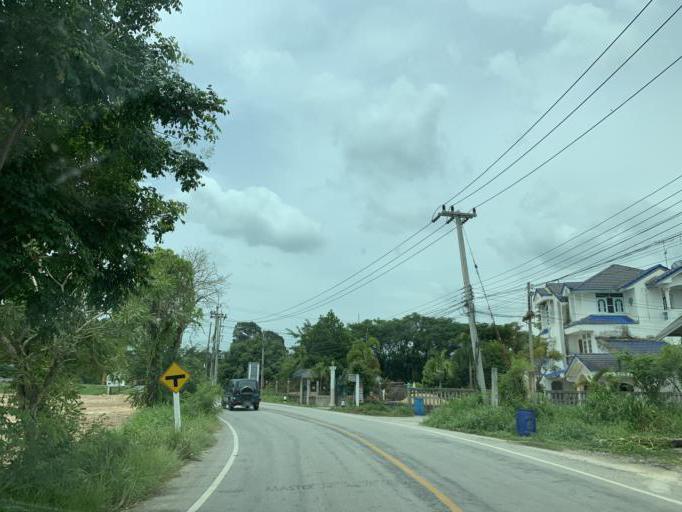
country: TH
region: Uthai Thani
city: Uthai Thani
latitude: 15.4020
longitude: 100.0284
